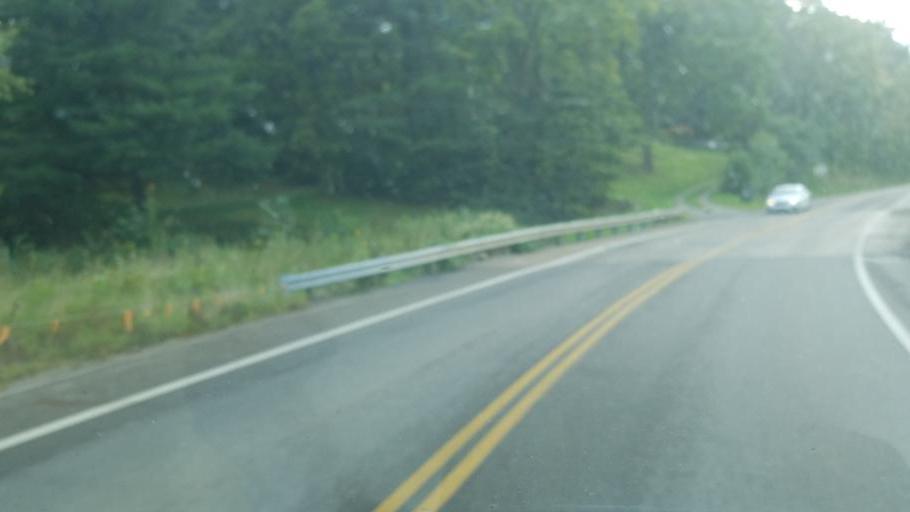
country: US
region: Ohio
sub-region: Holmes County
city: Millersburg
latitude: 40.5125
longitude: -81.9233
